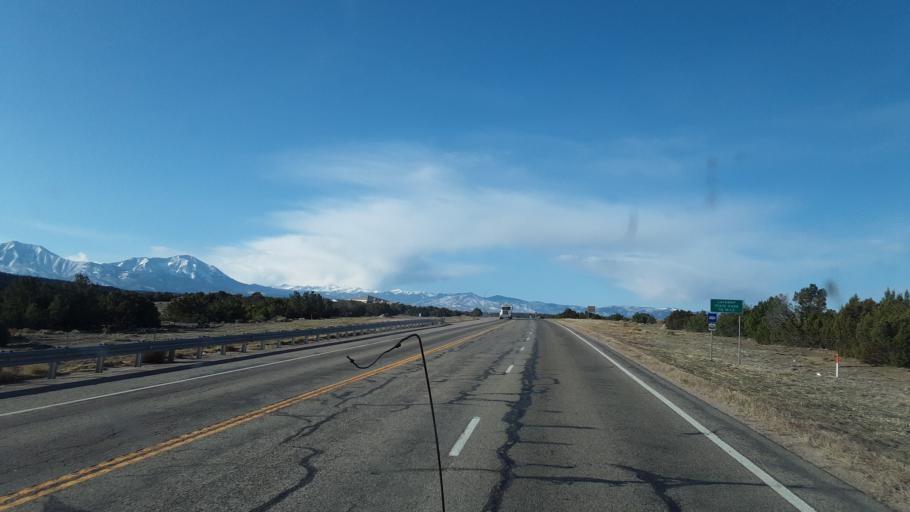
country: US
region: Colorado
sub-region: Huerfano County
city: Walsenburg
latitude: 37.6055
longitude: -104.8251
